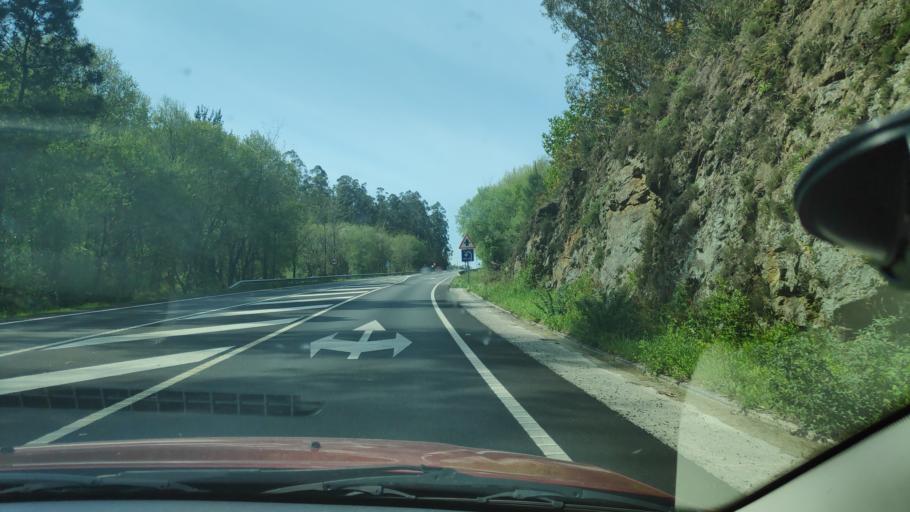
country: ES
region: Galicia
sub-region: Provincia da Coruna
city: Ames
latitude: 42.8769
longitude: -8.6739
